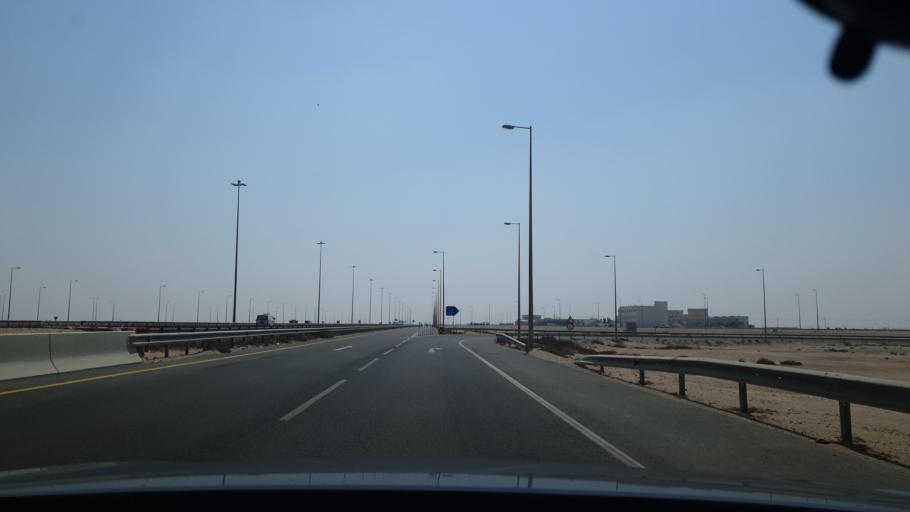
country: QA
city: Al Ghuwayriyah
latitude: 25.8289
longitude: 51.3496
